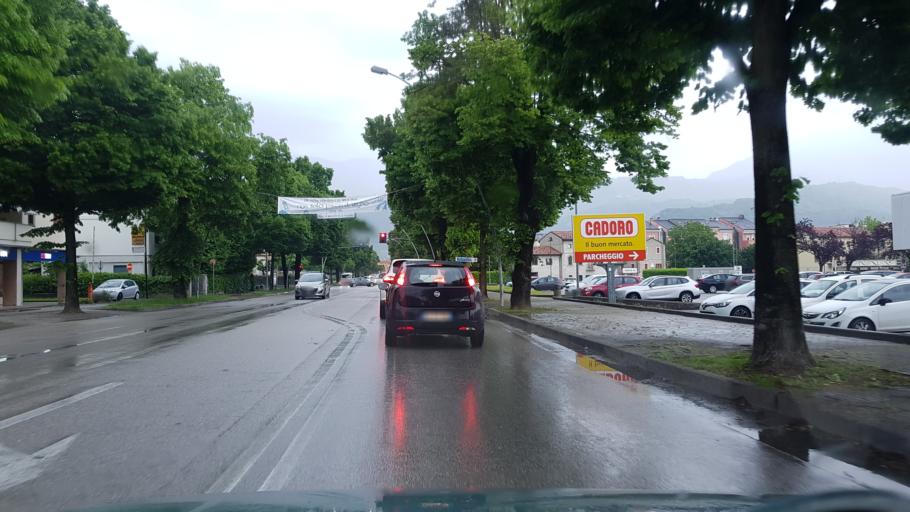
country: IT
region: Veneto
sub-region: Provincia di Treviso
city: Vittorio Veneto
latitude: 45.9755
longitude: 12.3077
